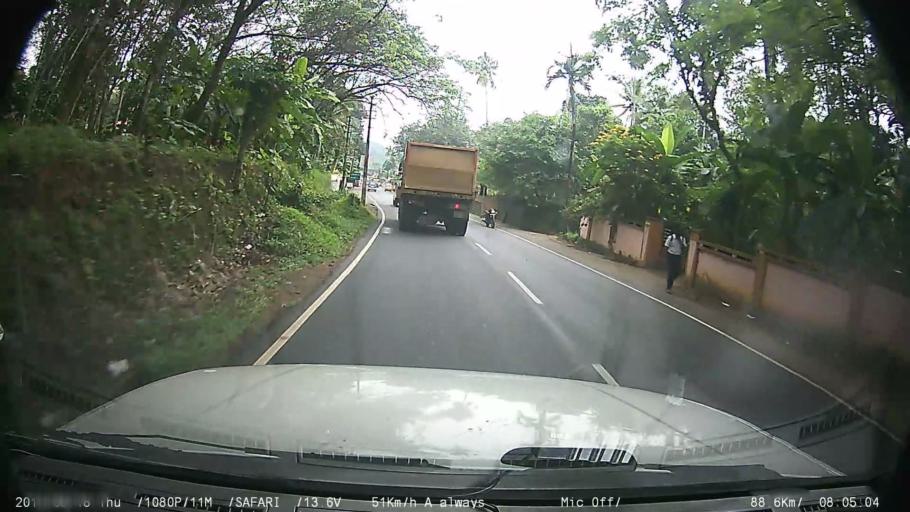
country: IN
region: Kerala
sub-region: Kottayam
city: Kottayam
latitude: 9.5838
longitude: 76.5826
